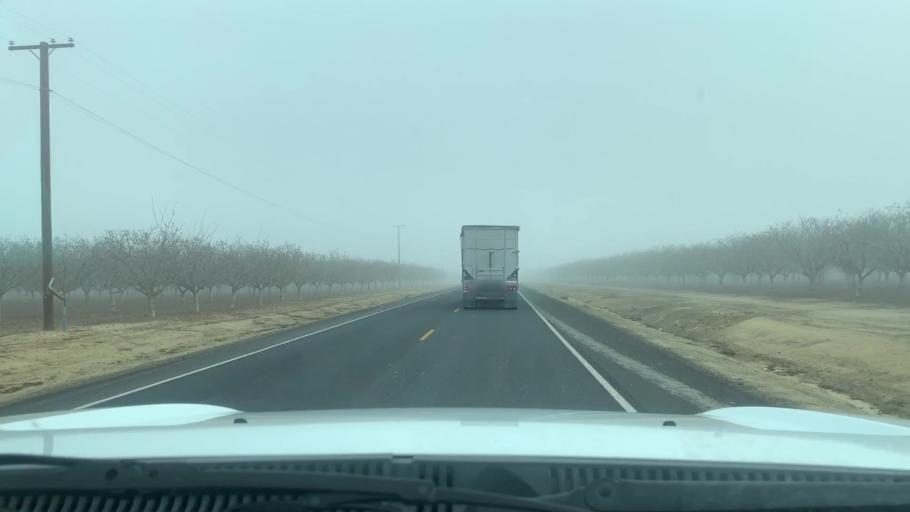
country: US
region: California
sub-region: Kern County
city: Lost Hills
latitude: 35.4993
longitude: -119.6390
